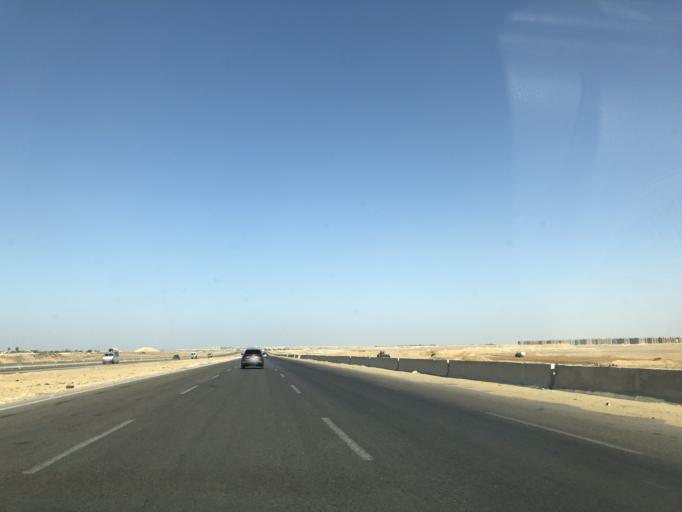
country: EG
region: Muhafazat al Minufiyah
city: Ashmun
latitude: 30.0677
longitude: 30.8741
